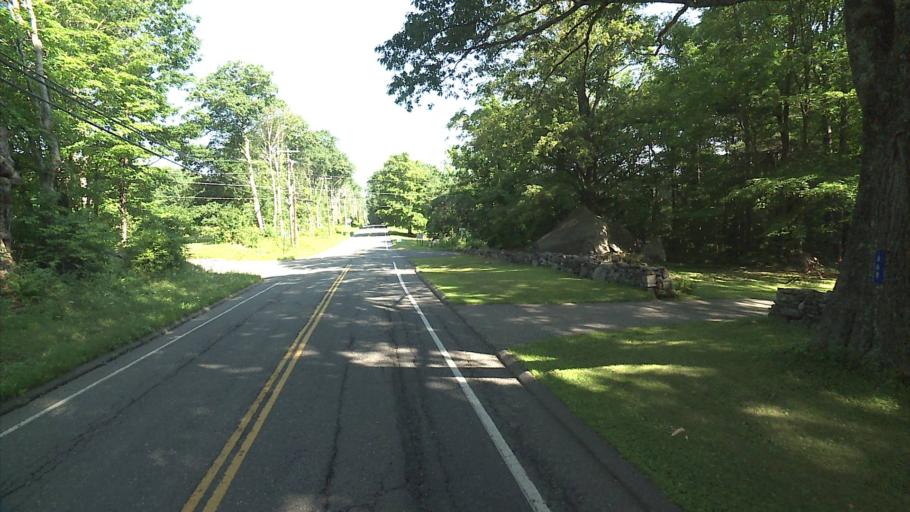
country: US
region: Connecticut
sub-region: Litchfield County
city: Winsted
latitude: 42.0066
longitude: -73.1071
